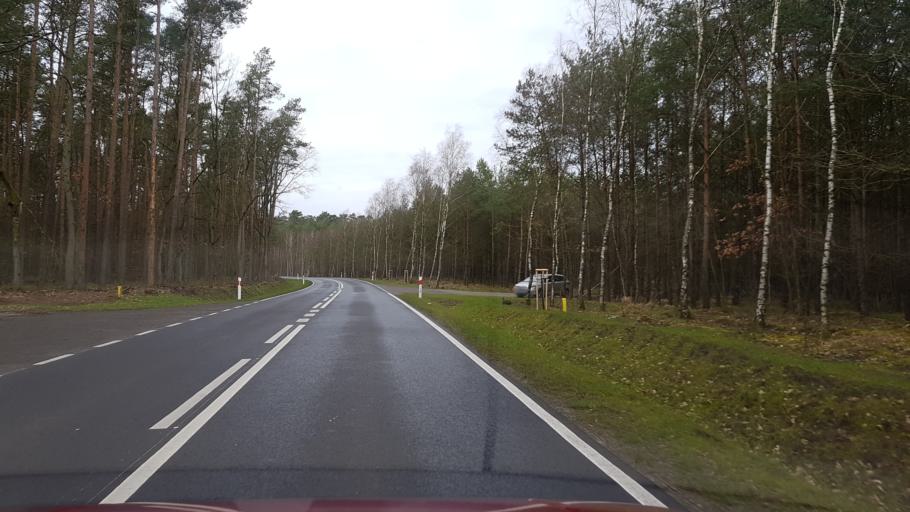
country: PL
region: West Pomeranian Voivodeship
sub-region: Powiat policki
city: Police
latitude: 53.6625
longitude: 14.4625
